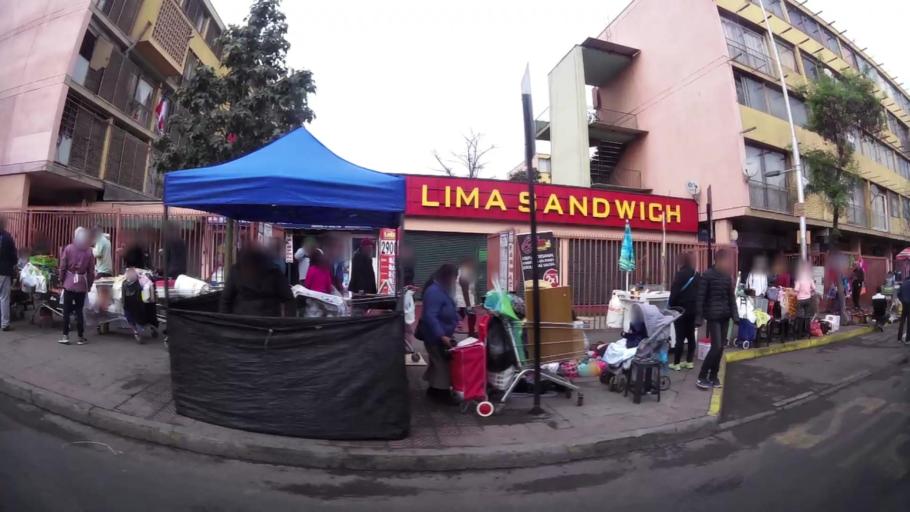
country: CL
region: Santiago Metropolitan
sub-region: Provincia de Santiago
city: Santiago
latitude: -33.4606
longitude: -70.6558
